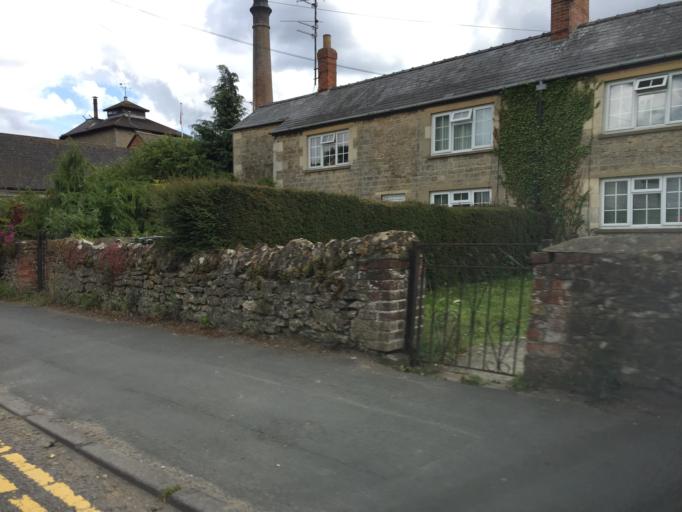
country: GB
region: England
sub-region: Borough of Swindon
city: Broad Blunsdon
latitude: 51.5929
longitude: -1.7629
